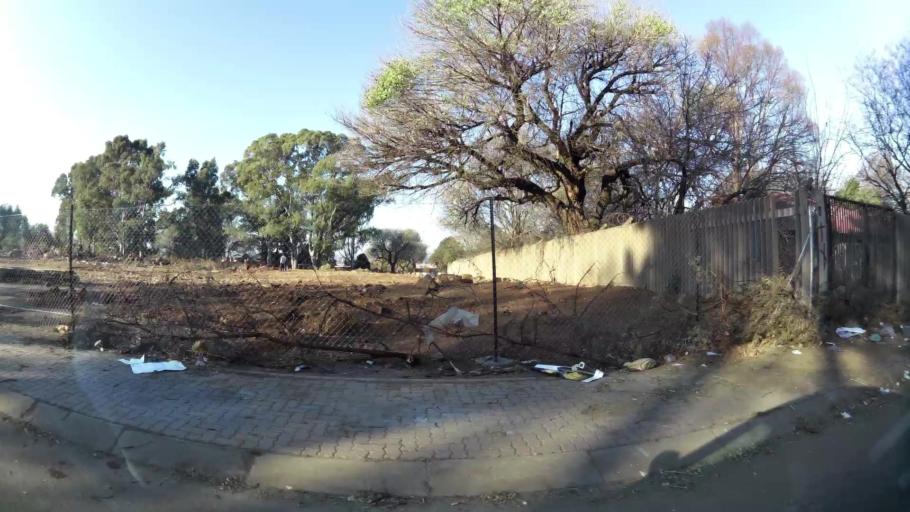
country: ZA
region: Gauteng
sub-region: City of Johannesburg Metropolitan Municipality
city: Soweto
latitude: -26.2584
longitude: 27.8838
